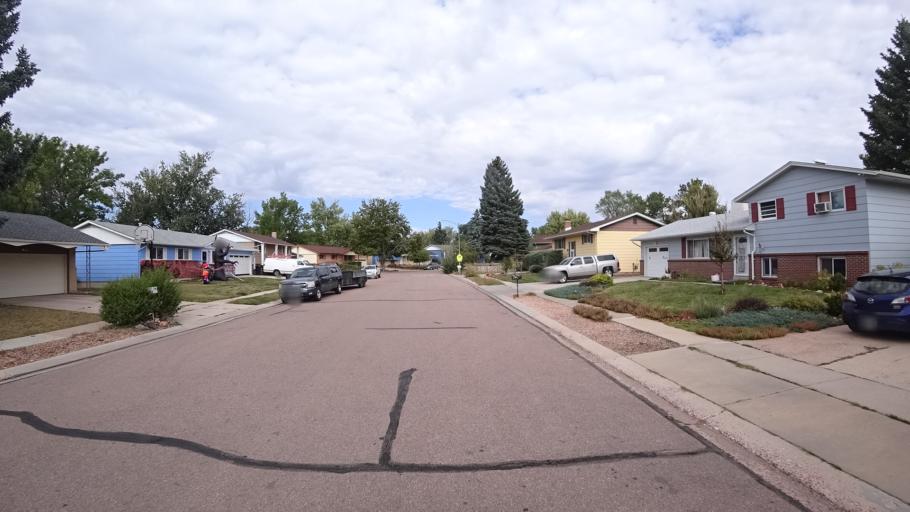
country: US
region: Colorado
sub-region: El Paso County
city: Cimarron Hills
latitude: 38.8512
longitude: -104.7462
